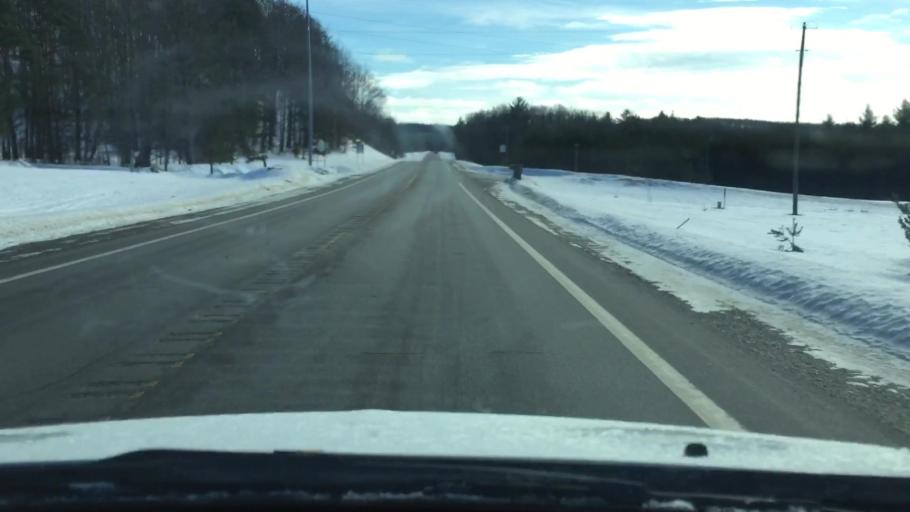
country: US
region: Michigan
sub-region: Antrim County
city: Mancelona
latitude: 44.9683
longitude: -85.0541
